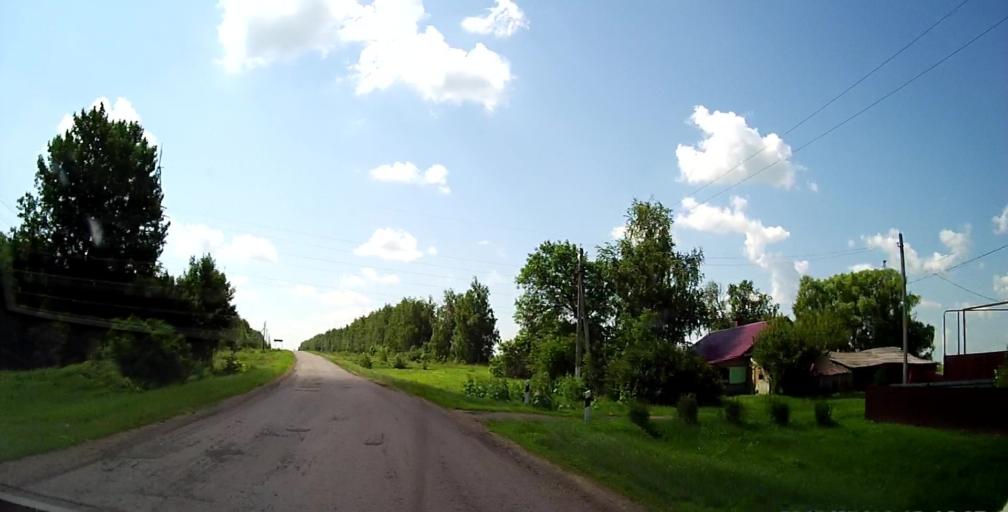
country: RU
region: Lipetsk
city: Chaplygin
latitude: 53.3685
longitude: 39.9163
